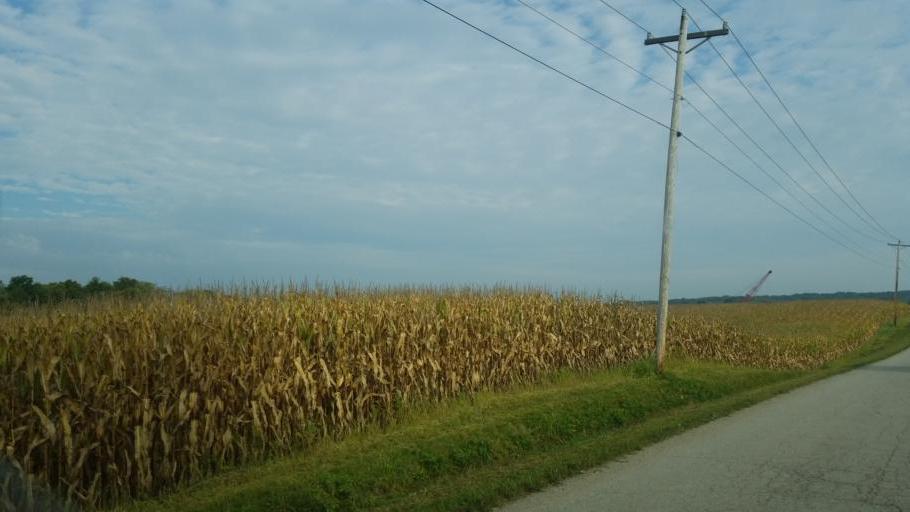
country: US
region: Ohio
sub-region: Knox County
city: Fredericktown
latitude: 40.4621
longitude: -82.6563
